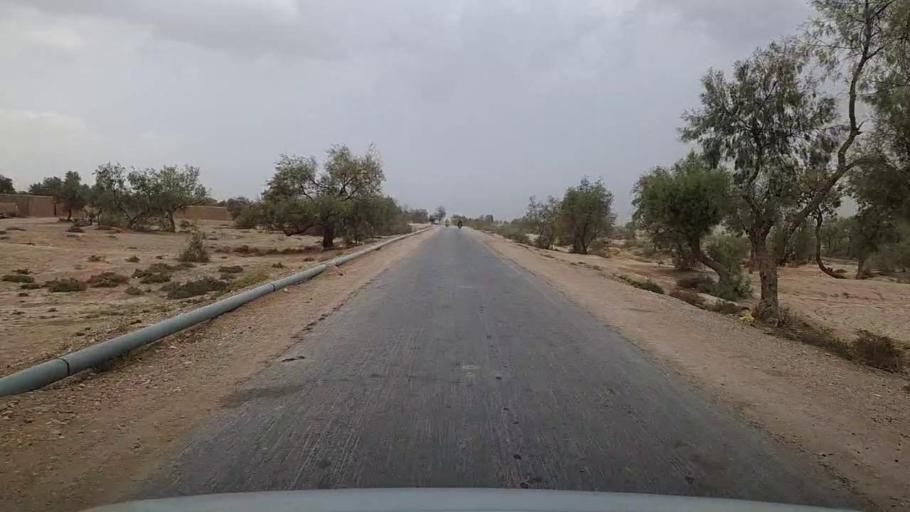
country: PK
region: Sindh
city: Sehwan
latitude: 26.3249
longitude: 67.7261
